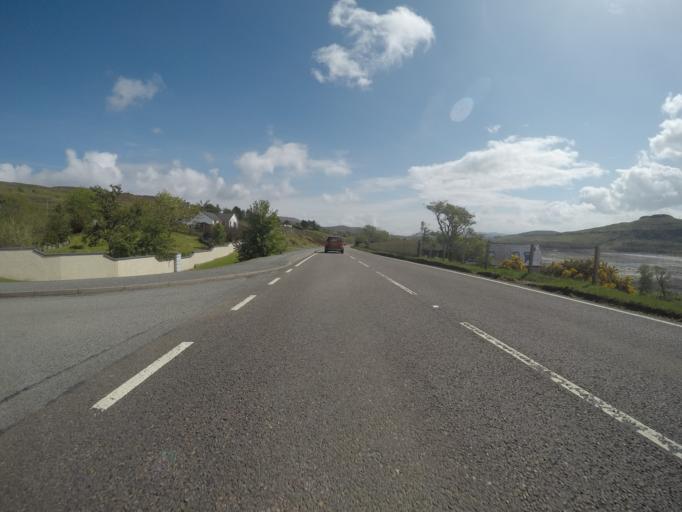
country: GB
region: Scotland
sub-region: Highland
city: Portree
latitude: 57.4890
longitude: -6.3138
